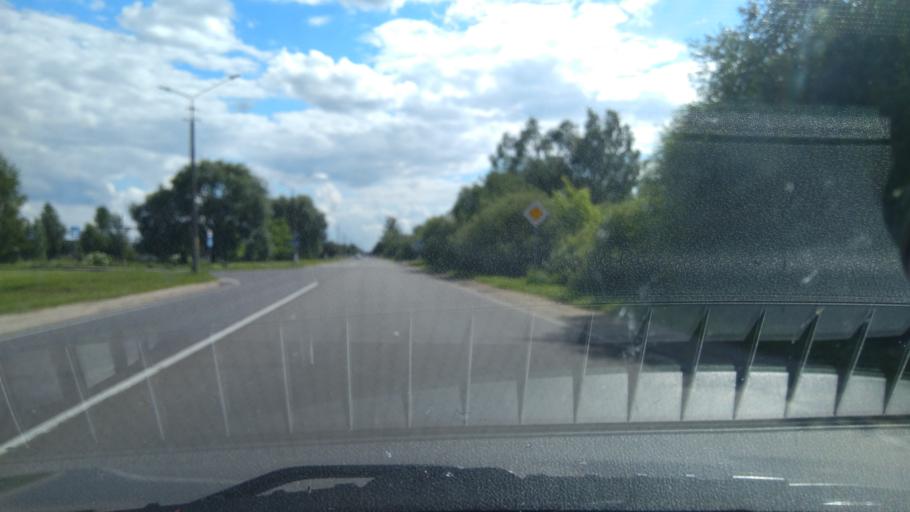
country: BY
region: Grodnenskaya
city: Masty
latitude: 53.4221
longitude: 24.5396
